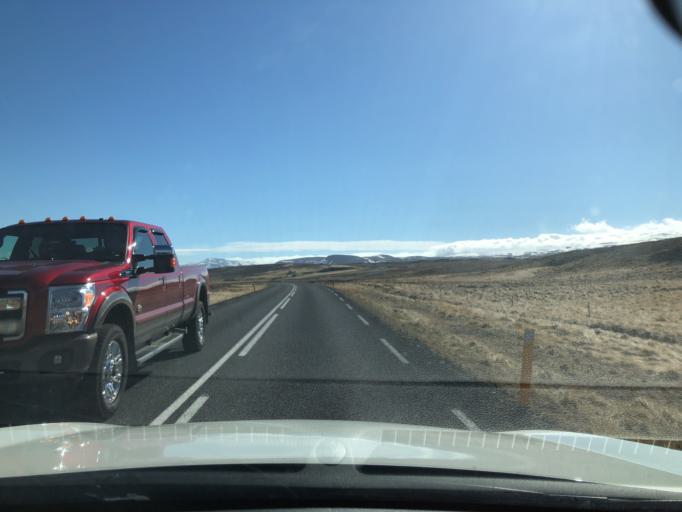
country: IS
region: South
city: Hveragerdi
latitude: 64.6990
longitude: -21.0694
